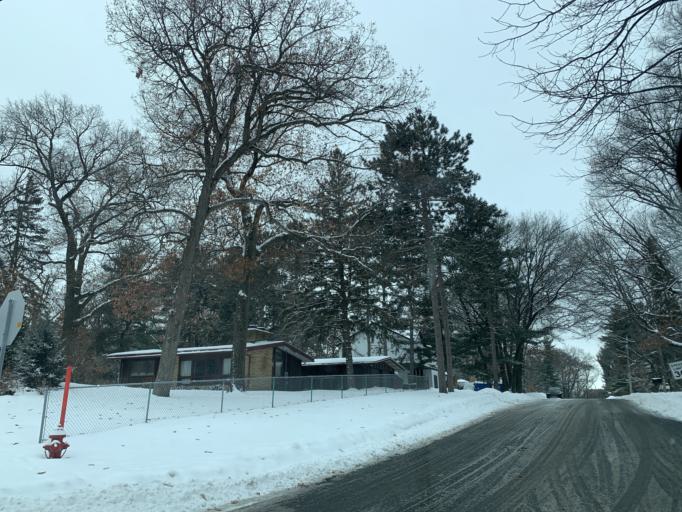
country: US
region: Minnesota
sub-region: Ramsey County
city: Little Canada
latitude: 45.0504
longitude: -93.1064
